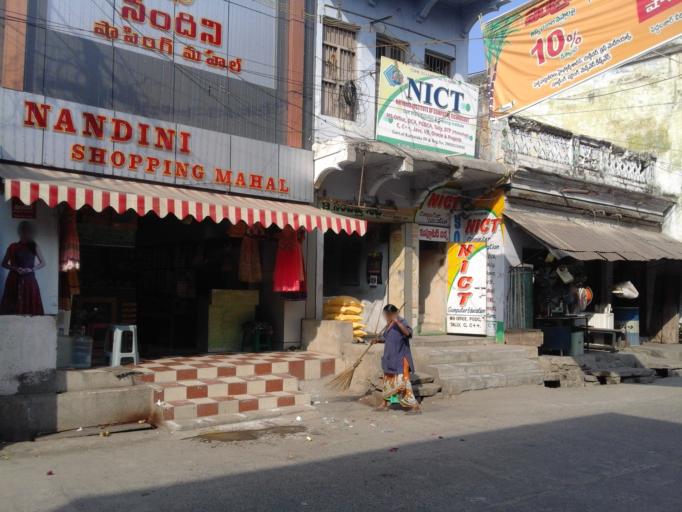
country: IN
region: Andhra Pradesh
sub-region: Chittoor
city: Chittoor
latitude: 13.2191
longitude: 79.0998
